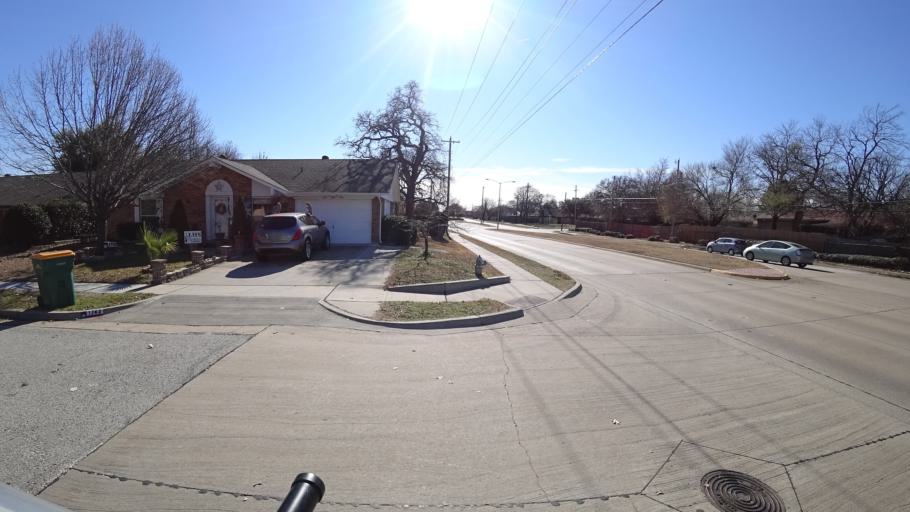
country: US
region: Texas
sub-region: Denton County
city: Lewisville
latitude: 33.0323
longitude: -97.0188
